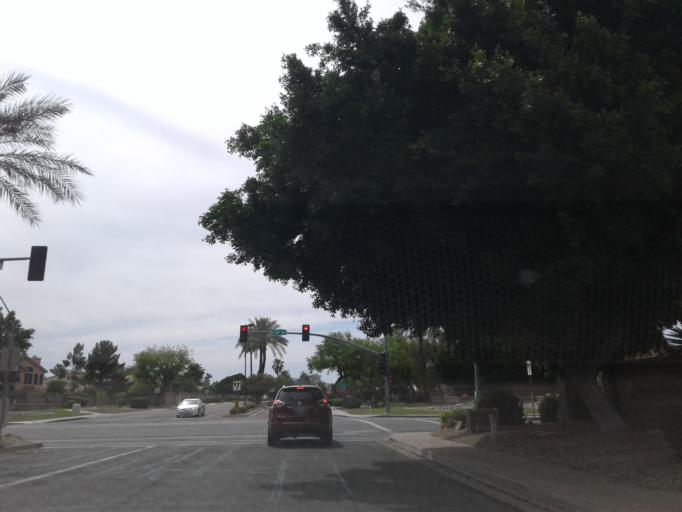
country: US
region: Arizona
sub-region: Maricopa County
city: Peoria
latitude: 33.6829
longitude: -112.1862
